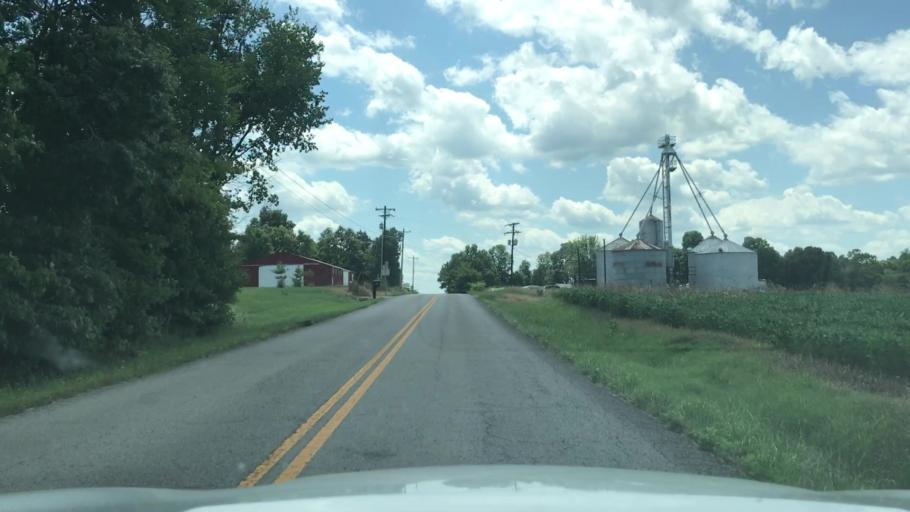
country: US
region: Kentucky
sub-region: Muhlenberg County
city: Greenville
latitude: 37.1651
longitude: -87.2483
